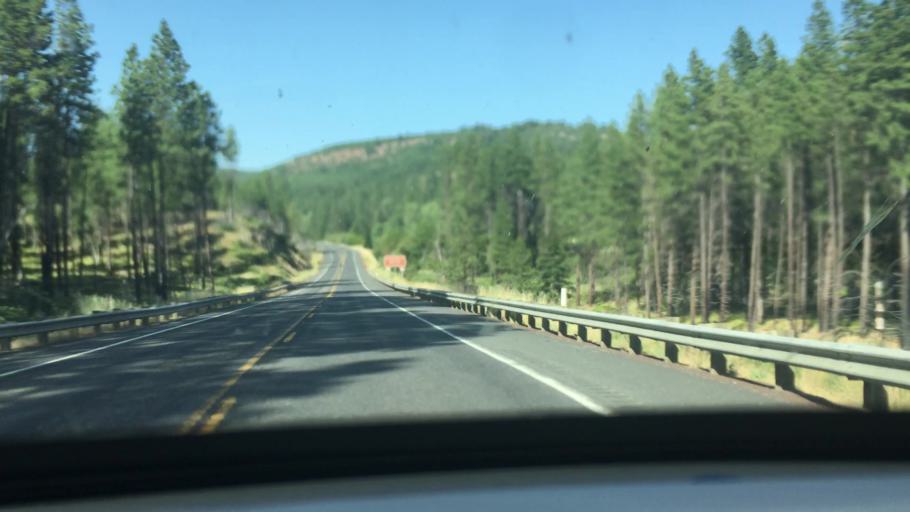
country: US
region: Washington
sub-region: Klickitat County
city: Goldendale
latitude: 45.9469
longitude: -120.6706
